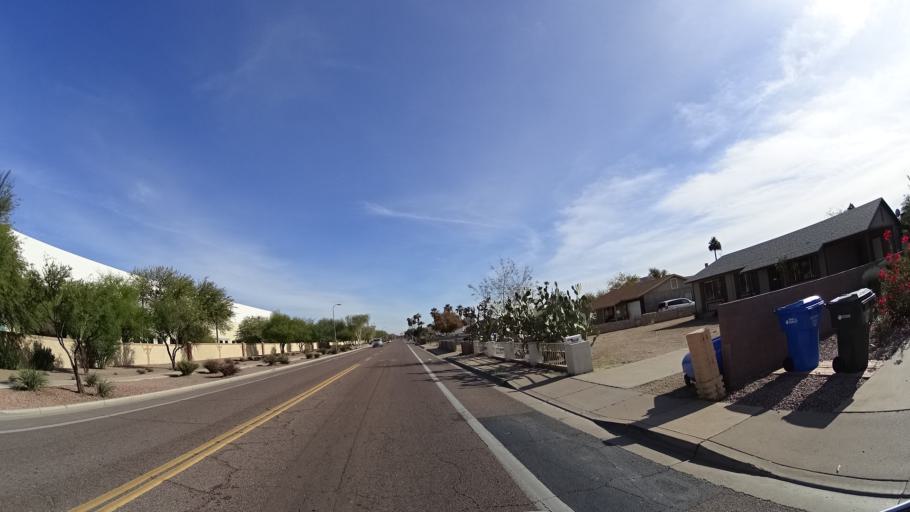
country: US
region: Arizona
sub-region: Maricopa County
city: Guadalupe
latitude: 33.3998
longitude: -111.9946
